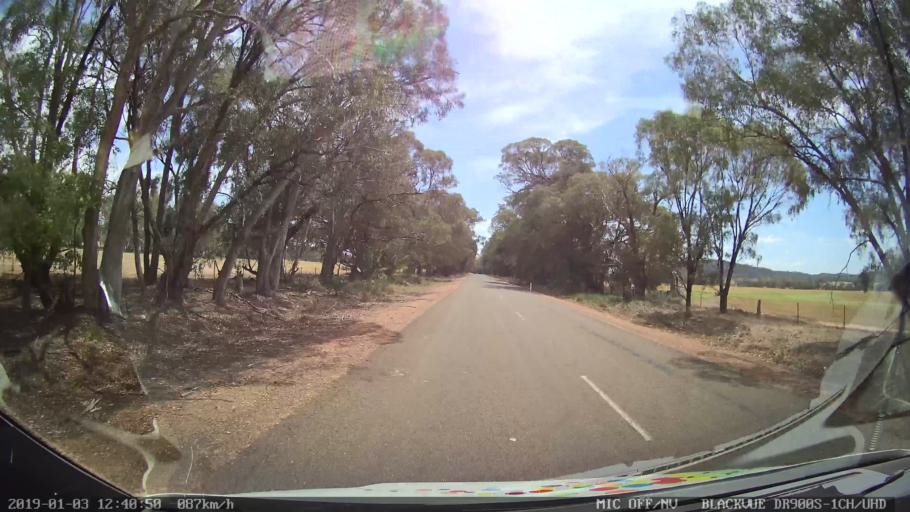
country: AU
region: New South Wales
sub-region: Weddin
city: Grenfell
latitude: -33.8076
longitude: 148.2137
